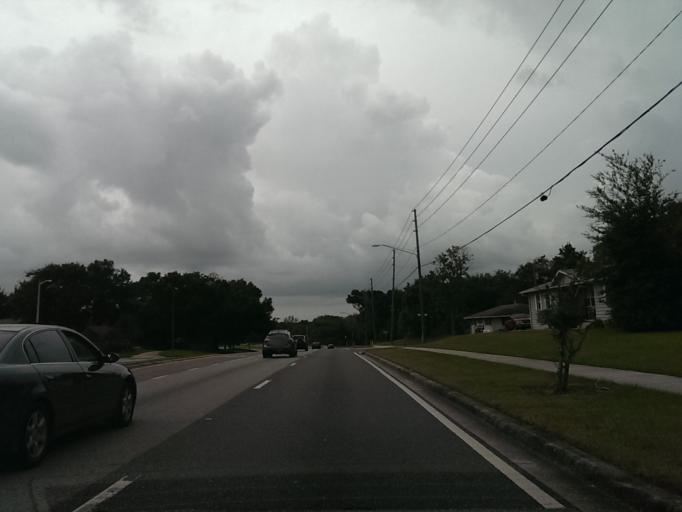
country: US
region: Florida
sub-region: Orange County
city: Orlovista
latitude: 28.5329
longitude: -81.4758
